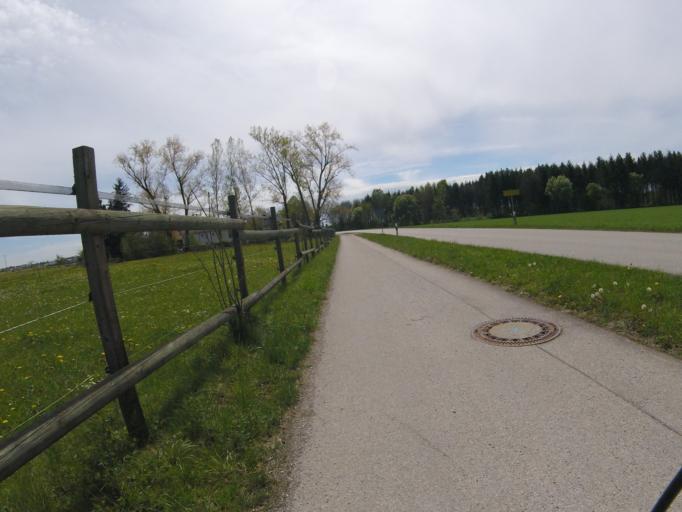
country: DE
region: Bavaria
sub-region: Upper Bavaria
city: Hohenkirchen-Siegertsbrunn
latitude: 48.0312
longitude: 11.7067
